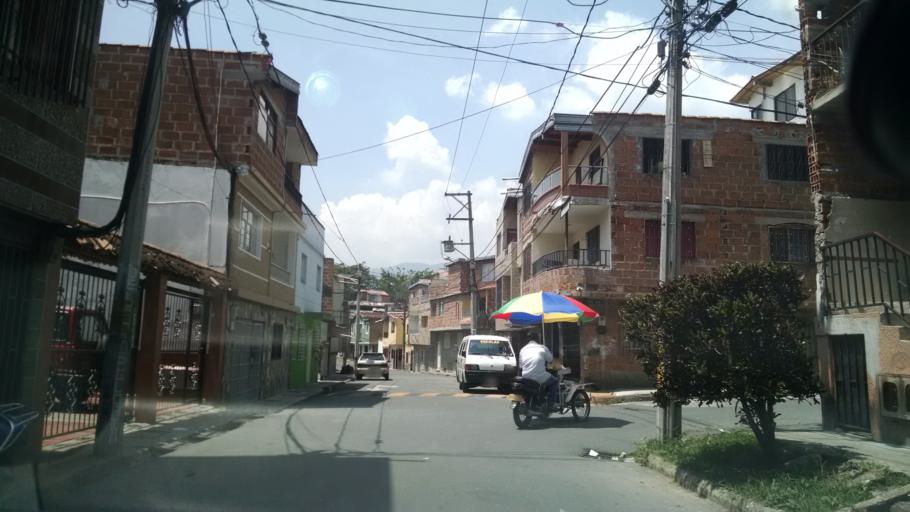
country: CO
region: Antioquia
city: Medellin
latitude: 6.2597
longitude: -75.6101
